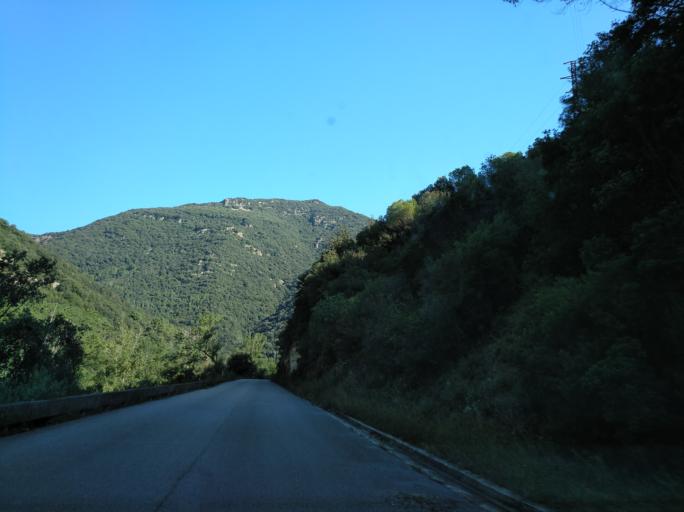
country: ES
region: Catalonia
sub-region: Provincia de Girona
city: Susqueda
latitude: 41.9872
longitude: 2.5708
